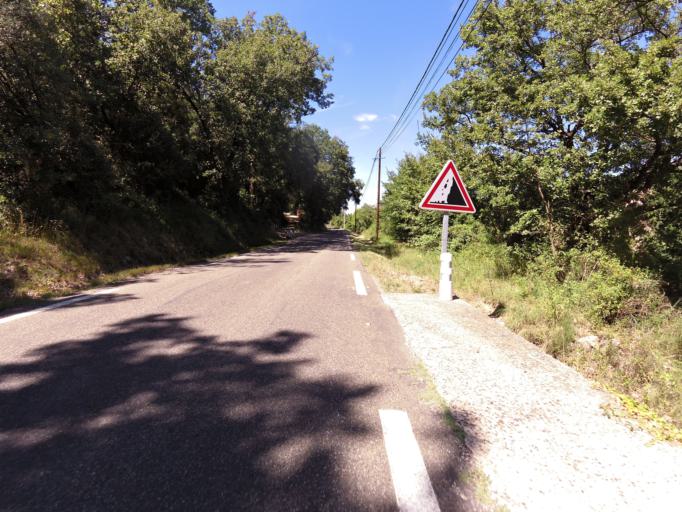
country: FR
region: Languedoc-Roussillon
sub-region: Departement du Gard
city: Sommieres
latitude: 43.8195
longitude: 4.0690
